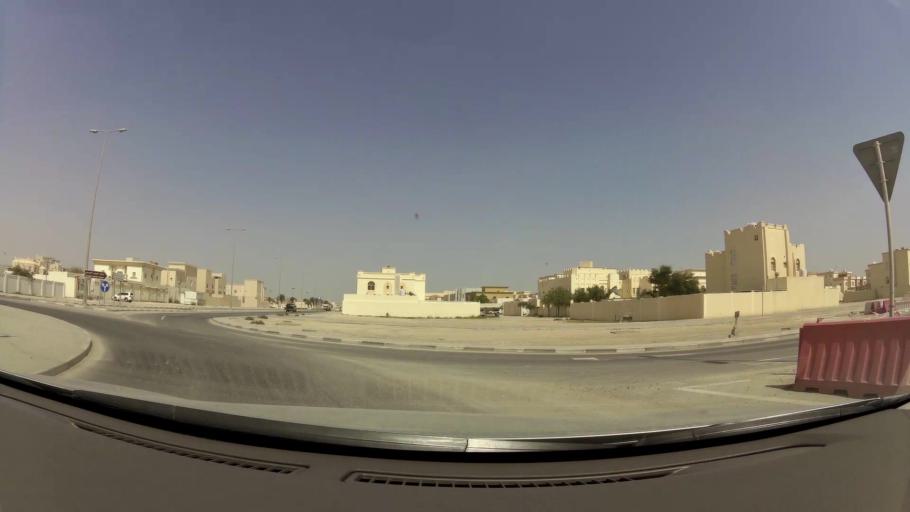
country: QA
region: Baladiyat Umm Salal
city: Umm Salal Muhammad
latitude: 25.3759
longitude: 51.4610
